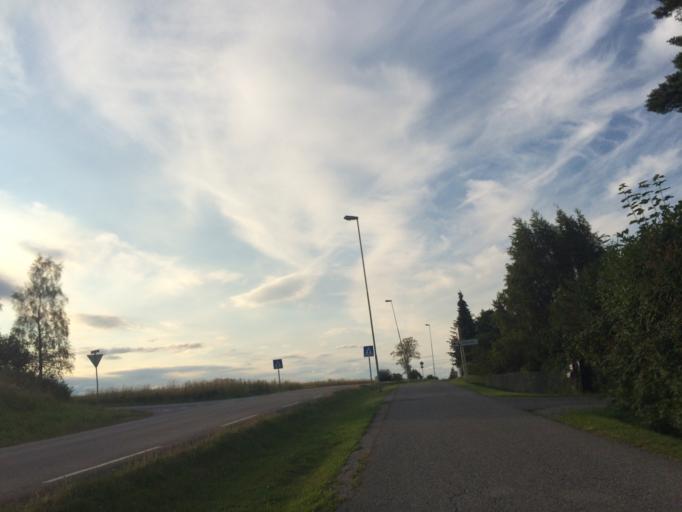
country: NO
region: Akershus
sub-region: Ski
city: Ski
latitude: 59.6762
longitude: 10.8857
